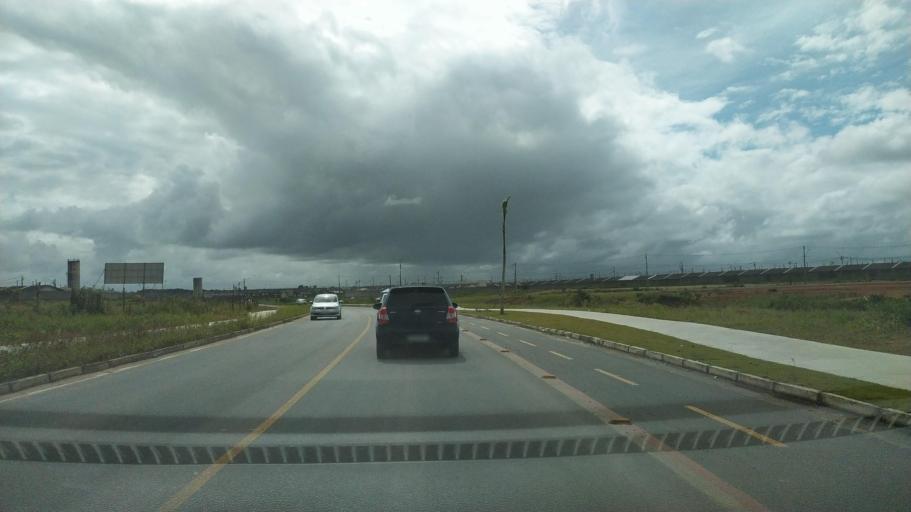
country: BR
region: Alagoas
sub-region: Satuba
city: Satuba
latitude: -9.5332
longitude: -35.7676
